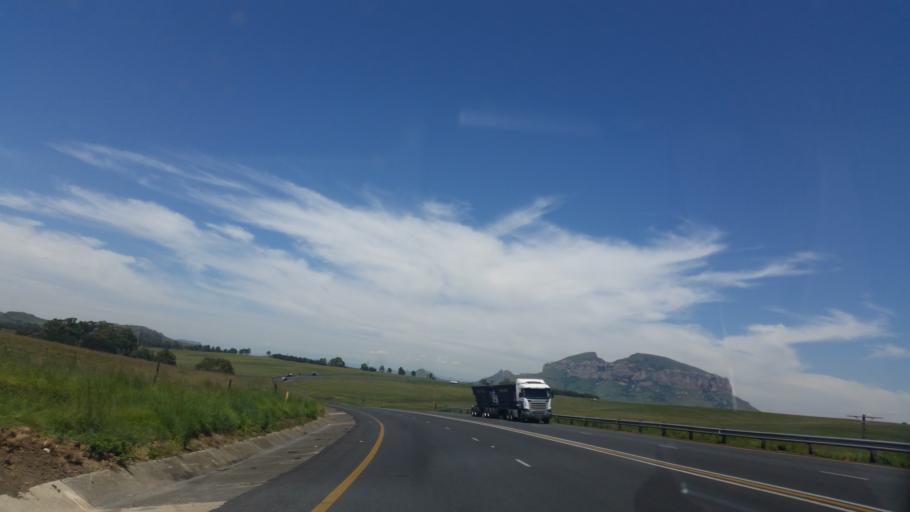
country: ZA
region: Orange Free State
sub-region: Thabo Mofutsanyana District Municipality
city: Harrismith
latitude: -28.3677
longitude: 29.3392
